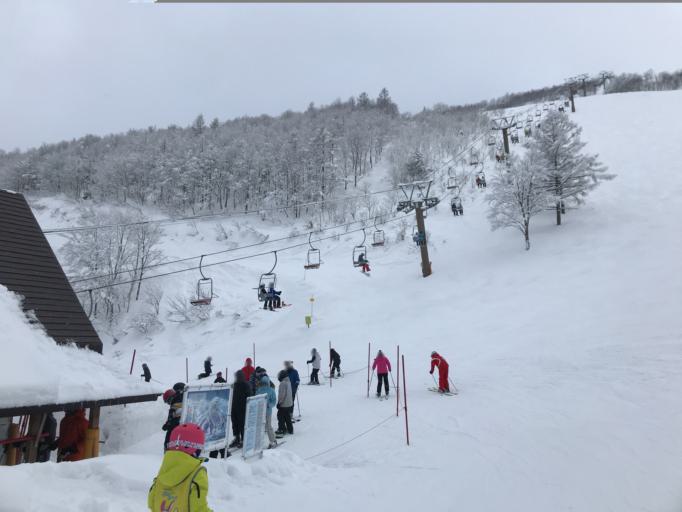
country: JP
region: Nagano
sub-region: Kitaazumi Gun
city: Hakuba
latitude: 36.7080
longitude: 137.8163
